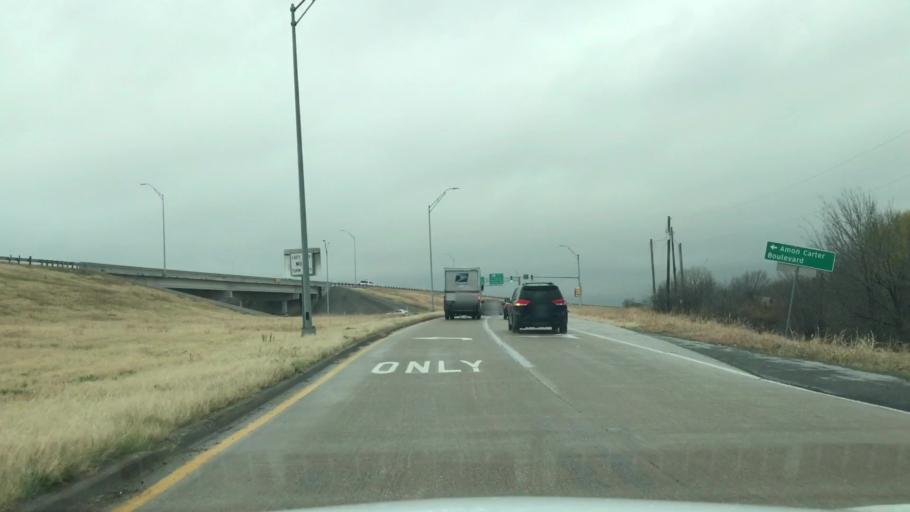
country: US
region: Texas
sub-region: Tarrant County
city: Euless
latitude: 32.8385
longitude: -97.0476
